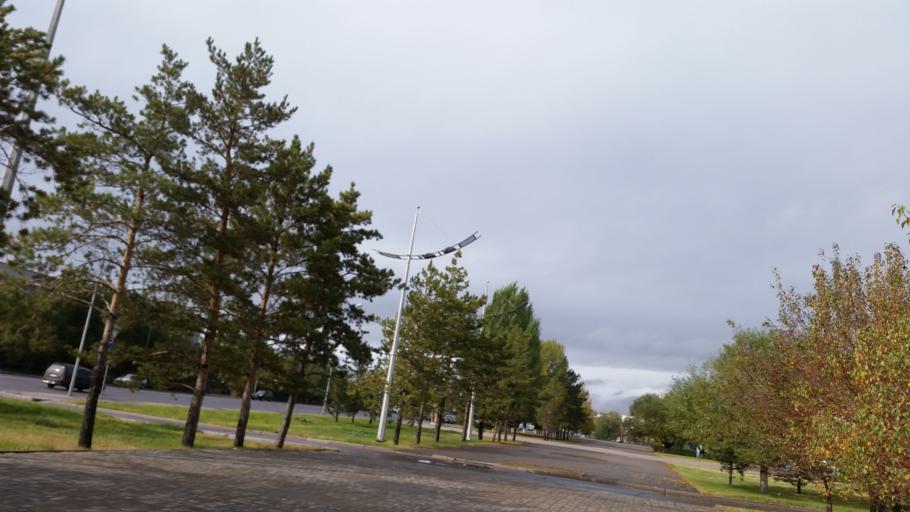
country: KZ
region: Astana Qalasy
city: Astana
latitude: 51.1527
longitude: 71.4560
